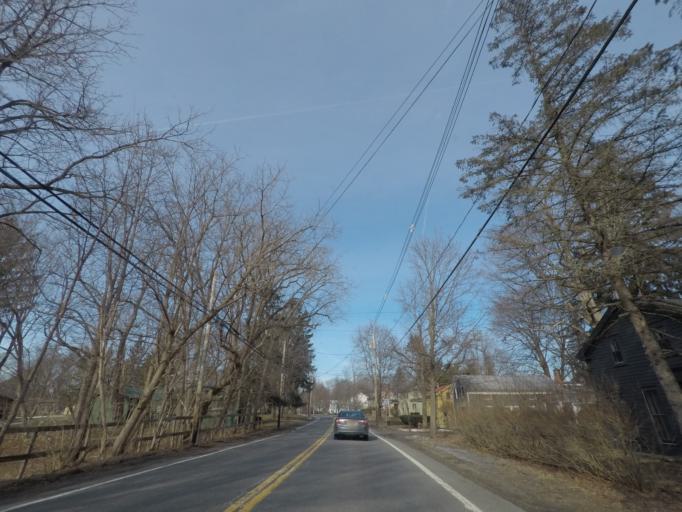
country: US
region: New York
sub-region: Columbia County
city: Niverville
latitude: 42.4688
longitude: -73.6318
